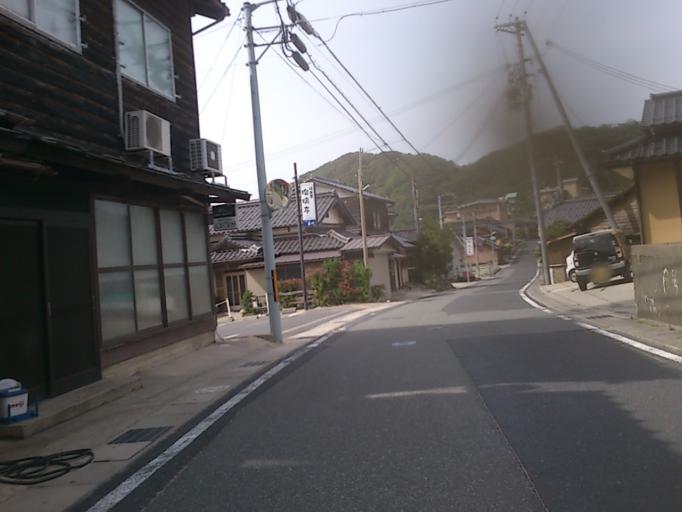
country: JP
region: Hyogo
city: Toyooka
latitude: 35.6655
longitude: 134.9679
